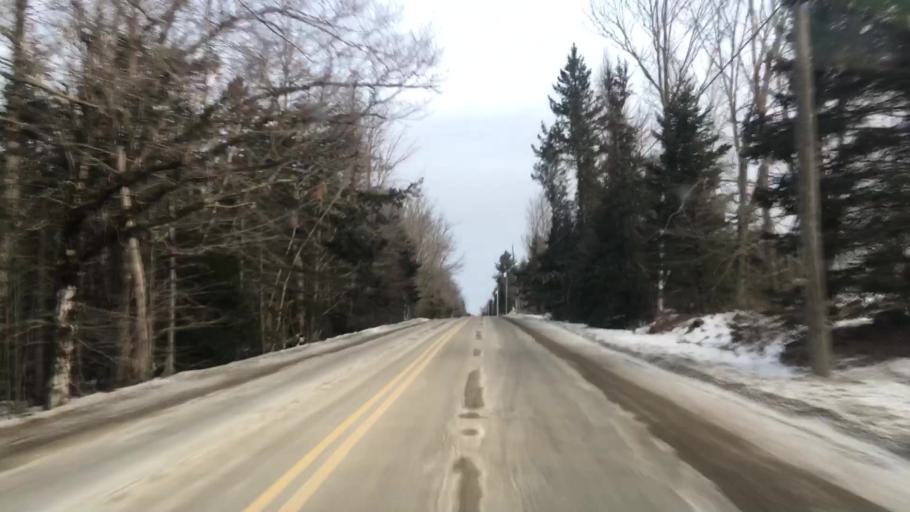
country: US
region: Maine
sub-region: Hancock County
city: Franklin
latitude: 44.7255
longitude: -68.3346
